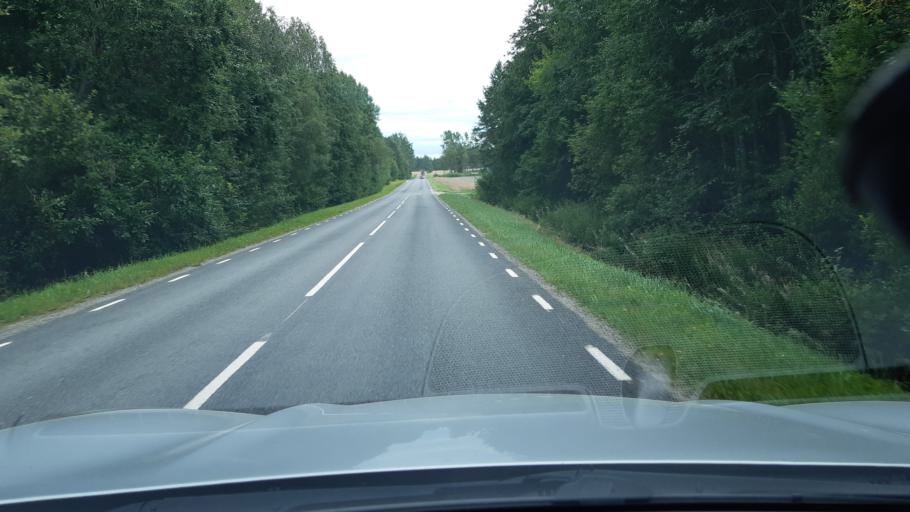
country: EE
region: Raplamaa
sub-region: Maerjamaa vald
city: Marjamaa
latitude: 59.0433
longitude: 24.4850
